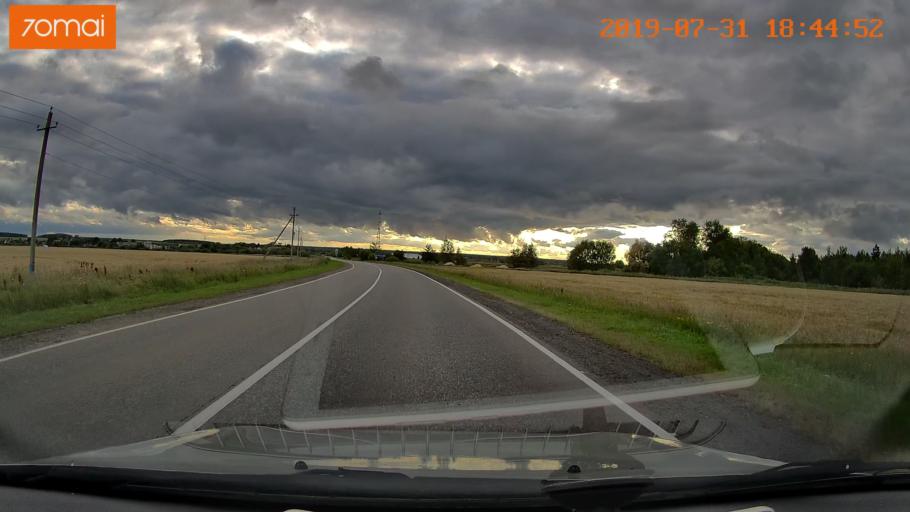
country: RU
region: Moskovskaya
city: Troitskoye
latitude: 55.2522
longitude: 38.5431
